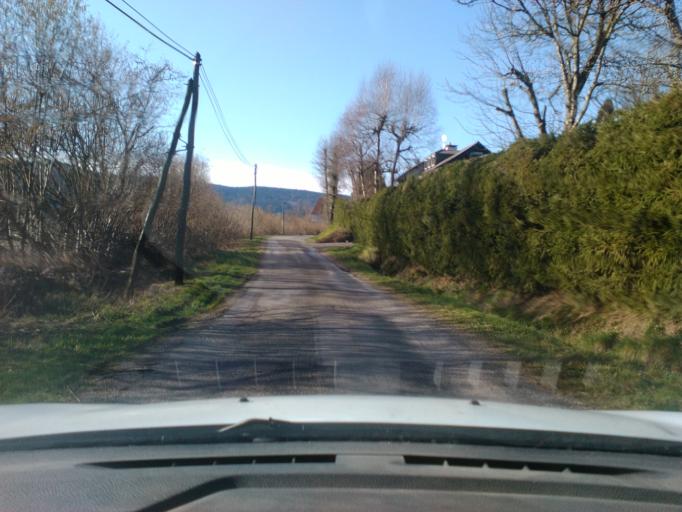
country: FR
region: Lorraine
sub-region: Departement des Vosges
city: Vecoux
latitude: 47.9770
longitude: 6.6492
